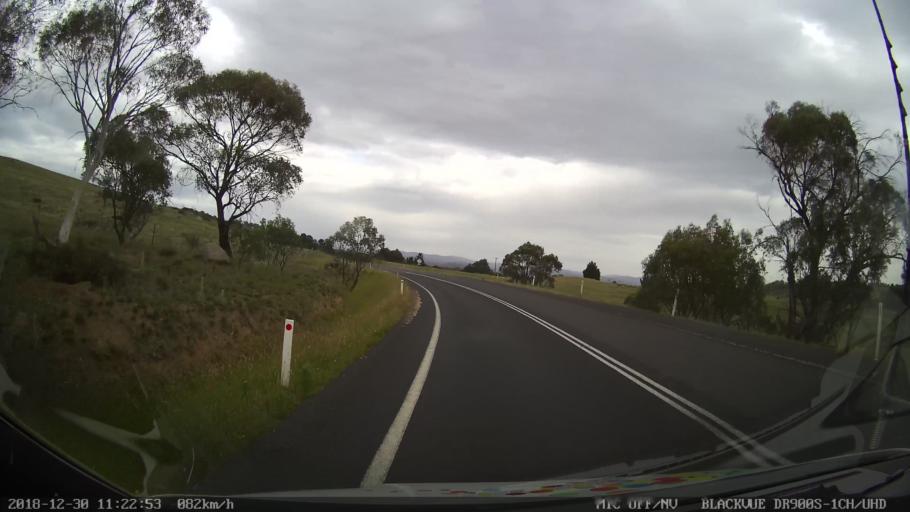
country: AU
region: New South Wales
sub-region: Snowy River
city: Jindabyne
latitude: -36.4943
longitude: 148.6697
